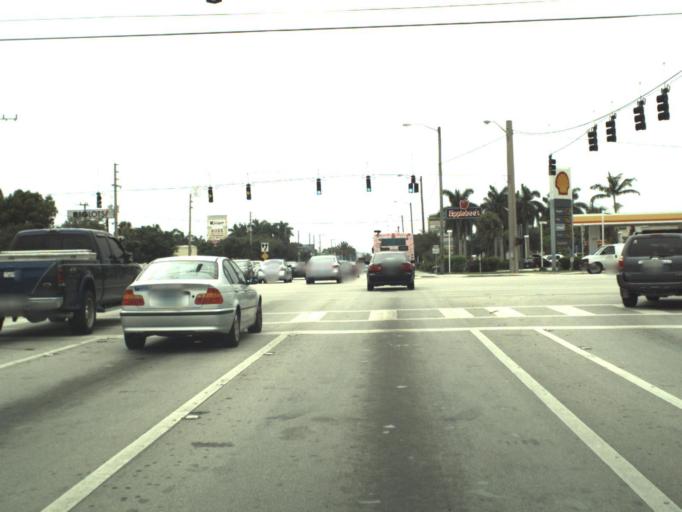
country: US
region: Florida
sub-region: Palm Beach County
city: Schall Circle
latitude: 26.7073
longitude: -80.1112
